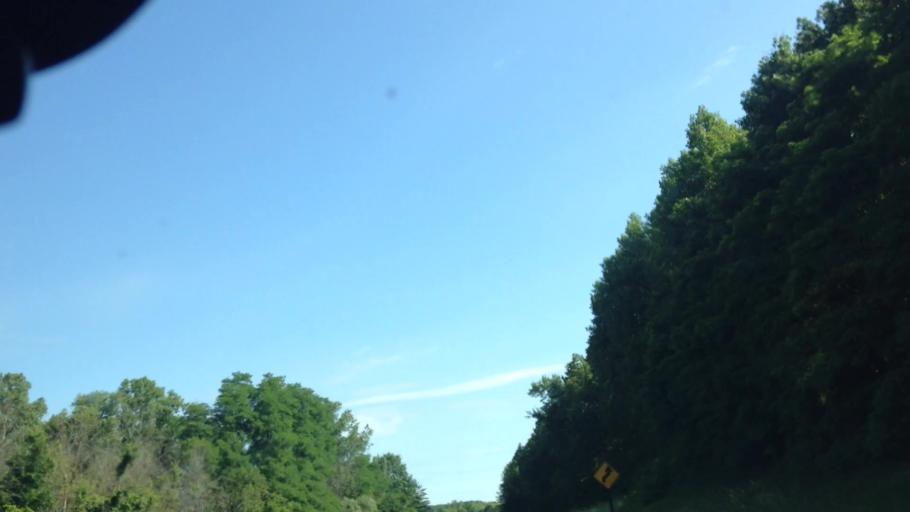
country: US
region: Wisconsin
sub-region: Washington County
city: Slinger
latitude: 43.3709
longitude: -88.2573
